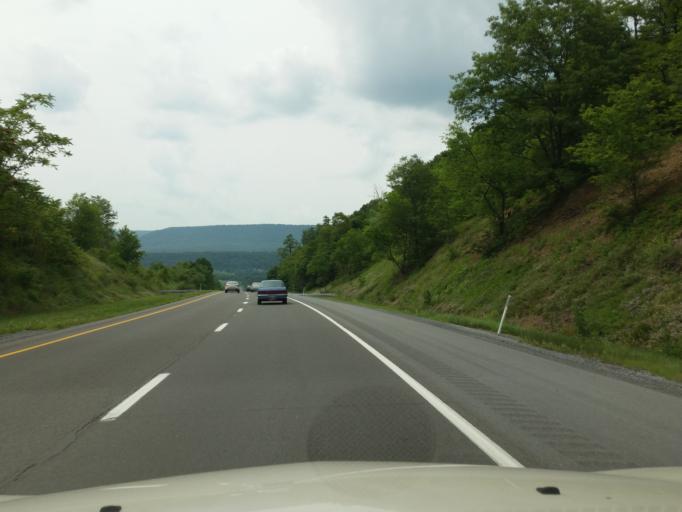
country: US
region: Pennsylvania
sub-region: Juniata County
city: Mifflintown
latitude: 40.5950
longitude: -77.3784
